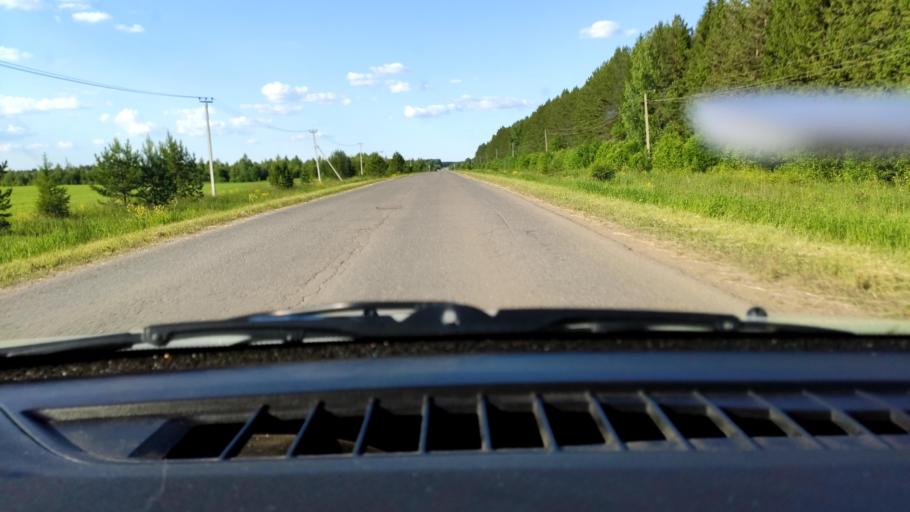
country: RU
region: Perm
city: Uinskoye
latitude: 57.1038
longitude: 56.6572
